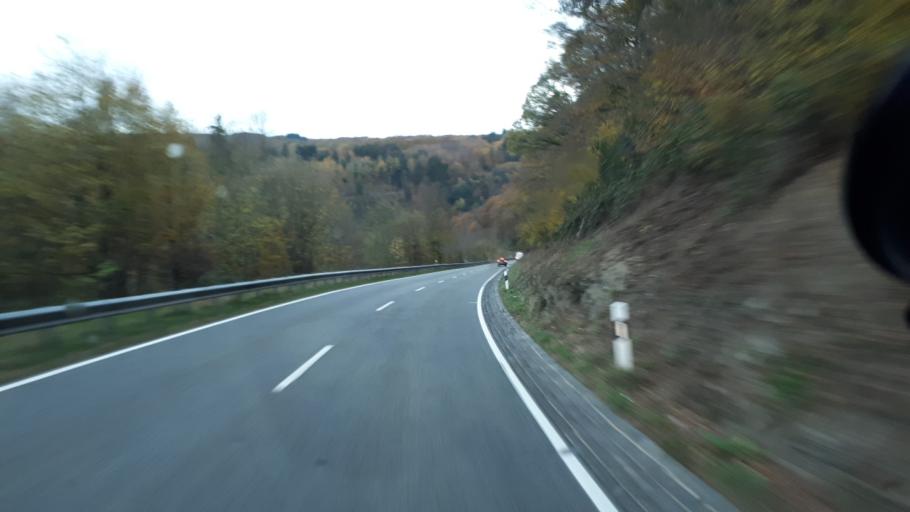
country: DE
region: Rheinland-Pfalz
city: Leienkaul
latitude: 50.2036
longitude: 7.0959
